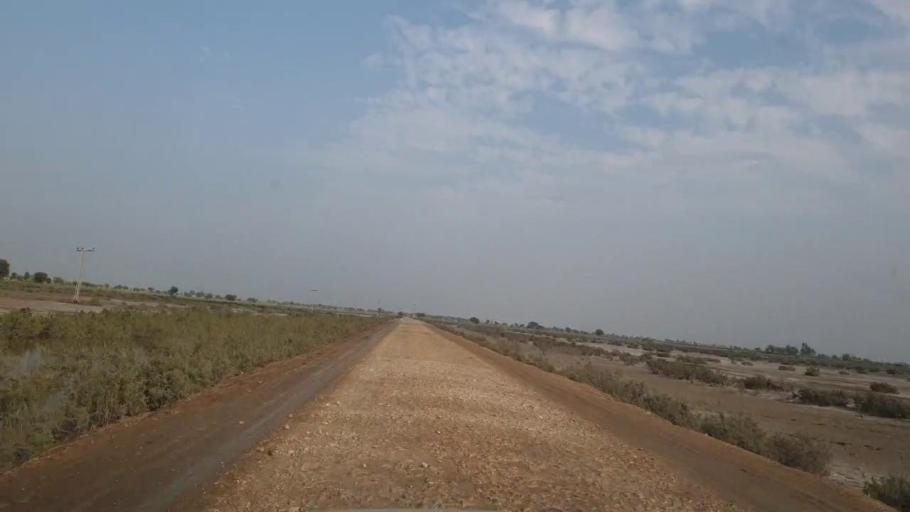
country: PK
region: Sindh
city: Mirpur Khas
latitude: 25.5628
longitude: 69.1954
